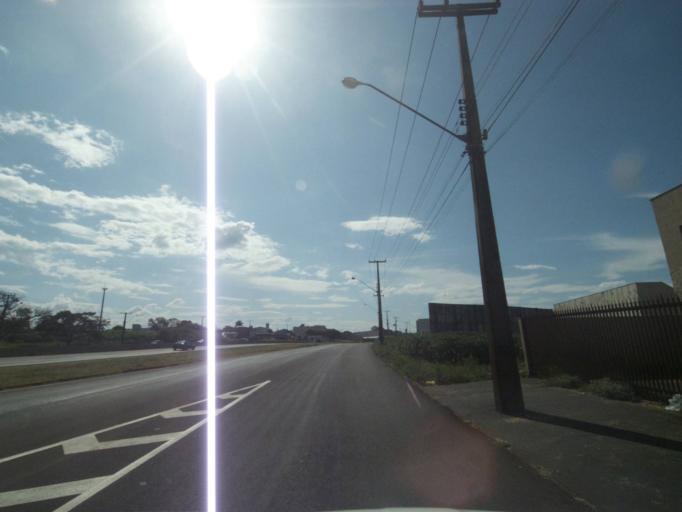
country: BR
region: Parana
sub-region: Londrina
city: Londrina
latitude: -23.3206
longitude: -51.2062
